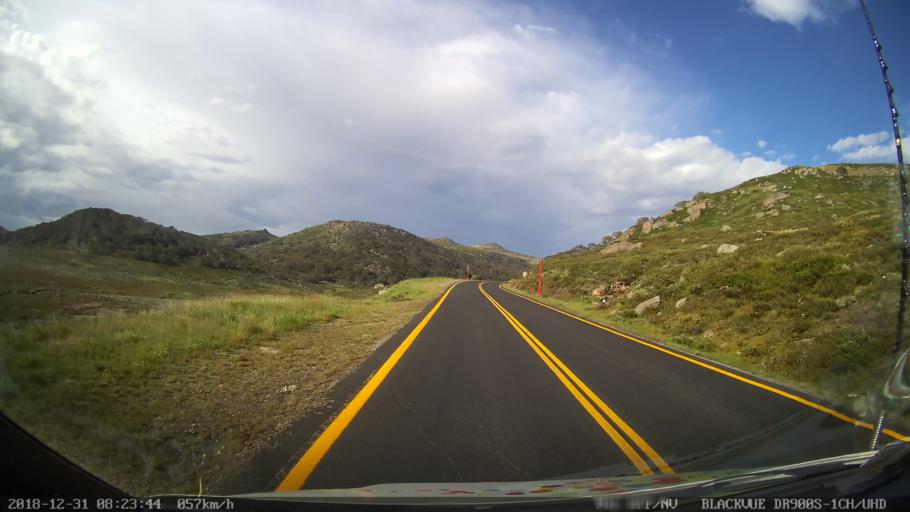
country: AU
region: New South Wales
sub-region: Snowy River
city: Jindabyne
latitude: -36.4286
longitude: 148.3475
